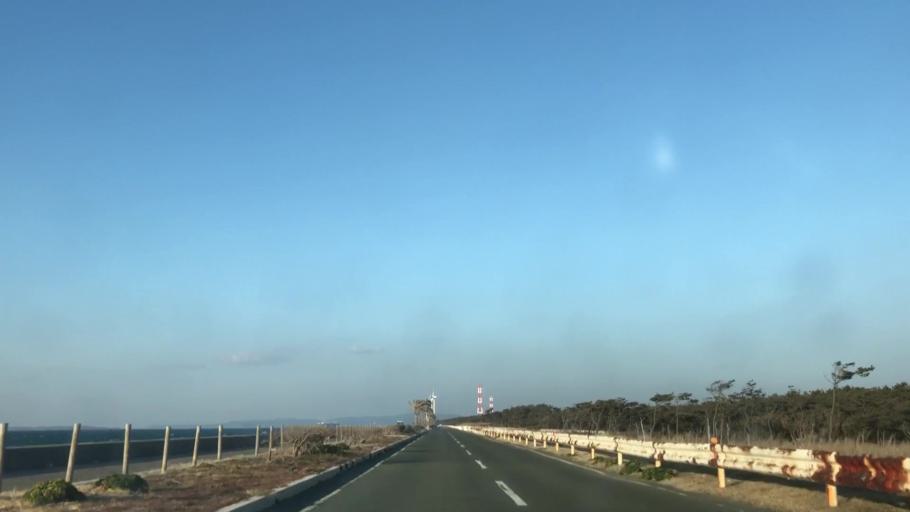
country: JP
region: Aichi
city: Toyohama
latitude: 34.6207
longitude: 137.0426
